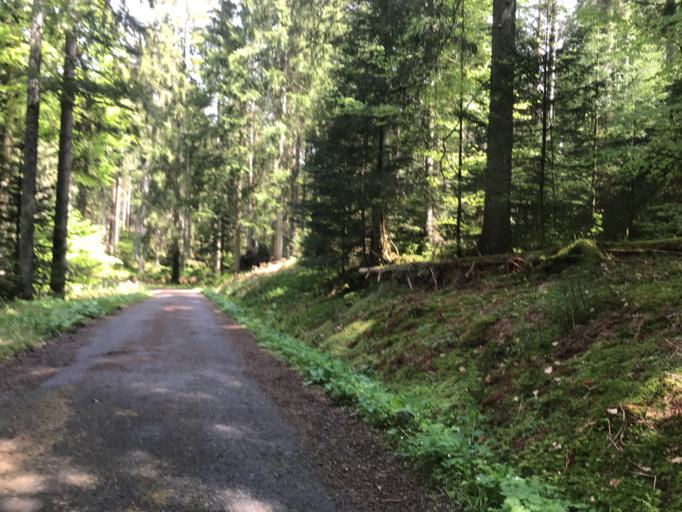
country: DE
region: Baden-Wuerttemberg
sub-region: Karlsruhe Region
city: Baiersbronn
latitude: 48.4791
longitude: 8.3372
